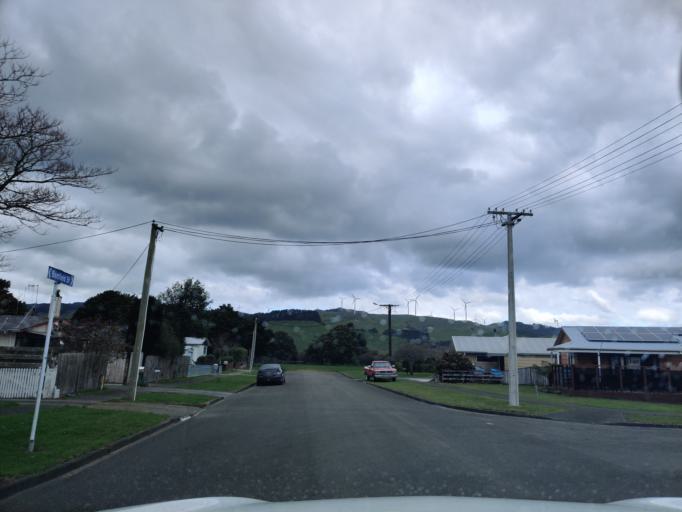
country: NZ
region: Manawatu-Wanganui
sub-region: Palmerston North City
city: Palmerston North
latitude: -40.2895
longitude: 175.7599
